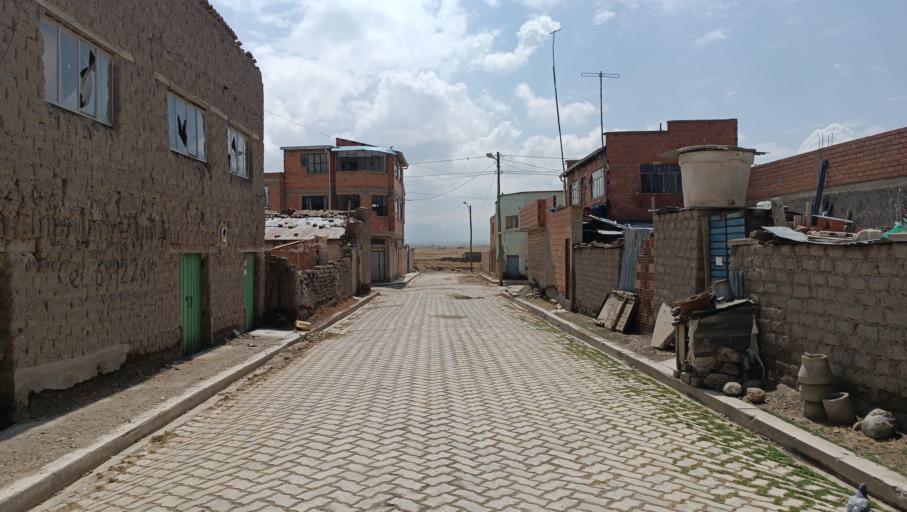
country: BO
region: La Paz
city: Batallas
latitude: -16.3977
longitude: -68.4782
